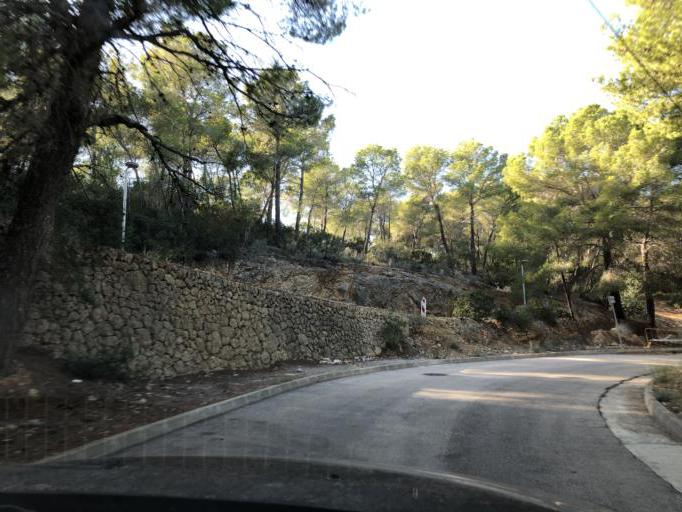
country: ES
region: Balearic Islands
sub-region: Illes Balears
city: Camp de Mar
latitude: 39.5389
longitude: 2.4081
